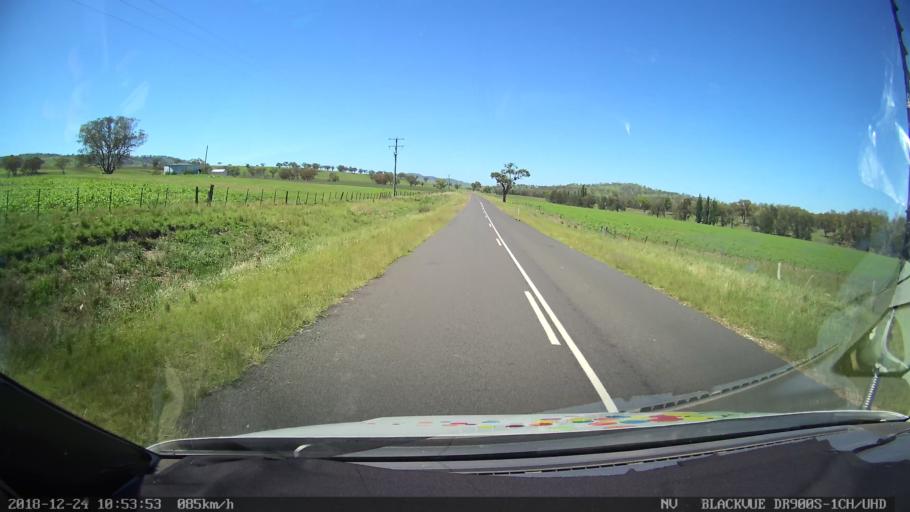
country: AU
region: New South Wales
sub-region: Upper Hunter Shire
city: Merriwa
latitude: -31.9969
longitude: 150.4192
